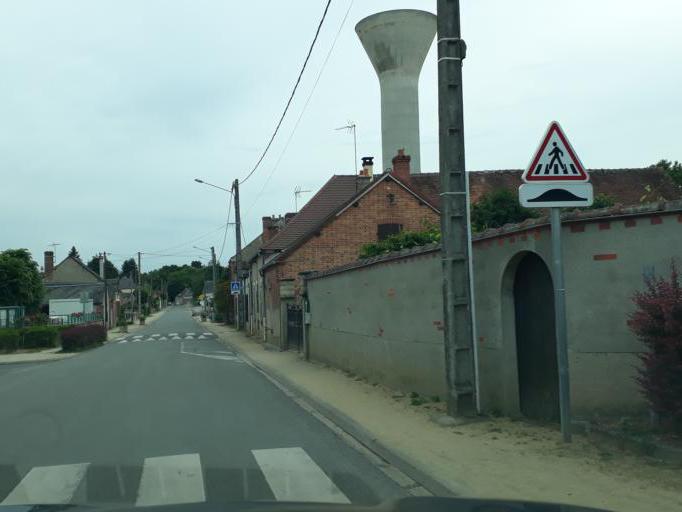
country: FR
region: Centre
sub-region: Departement du Loiret
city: Saint-Pere-sur-Loire
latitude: 47.7283
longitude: 2.3020
